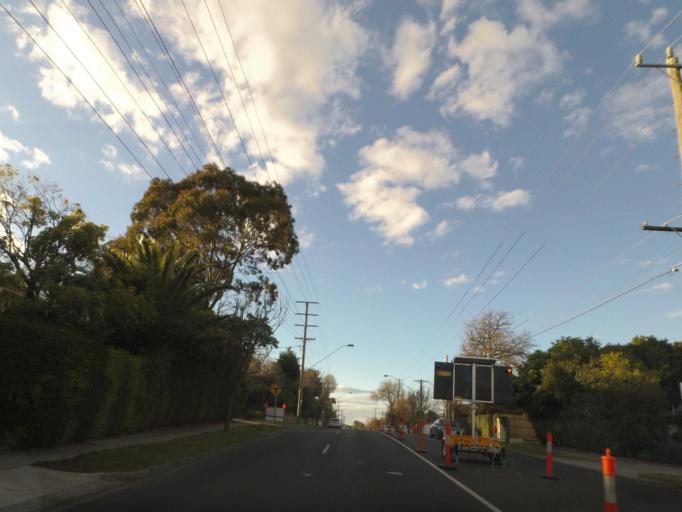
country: AU
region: Victoria
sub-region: Whitehorse
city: Surrey Hills
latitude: -37.8287
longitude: 145.0994
